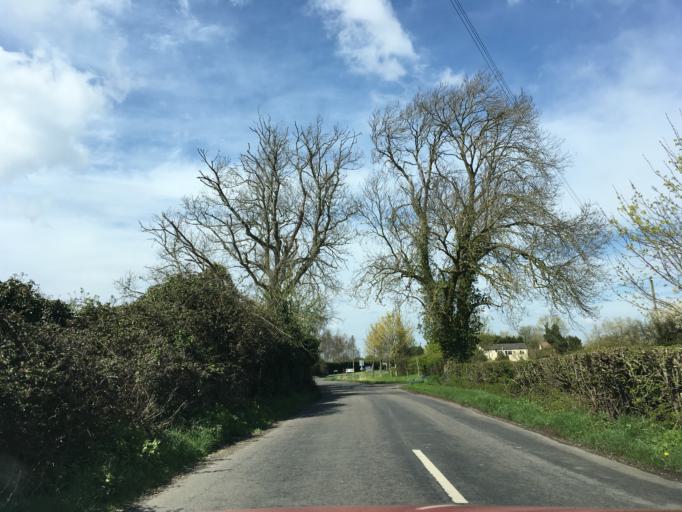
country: GB
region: England
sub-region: South Gloucestershire
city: Severn Beach
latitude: 51.5565
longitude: -2.6244
